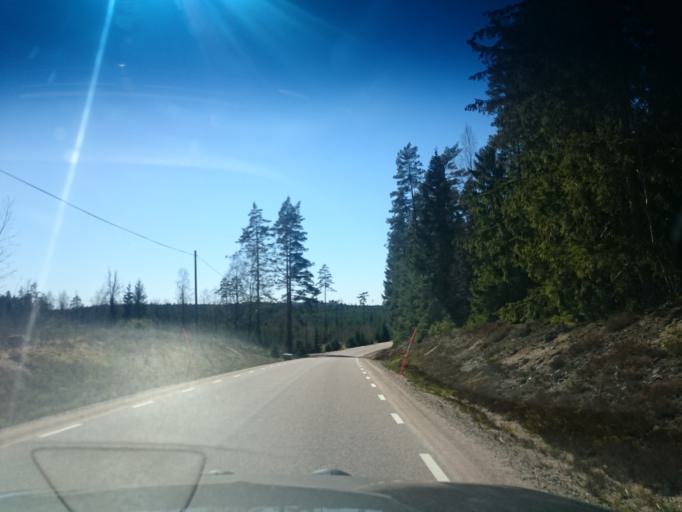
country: SE
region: Joenkoeping
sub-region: Vetlanda Kommun
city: Landsbro
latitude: 57.2250
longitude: 14.9808
